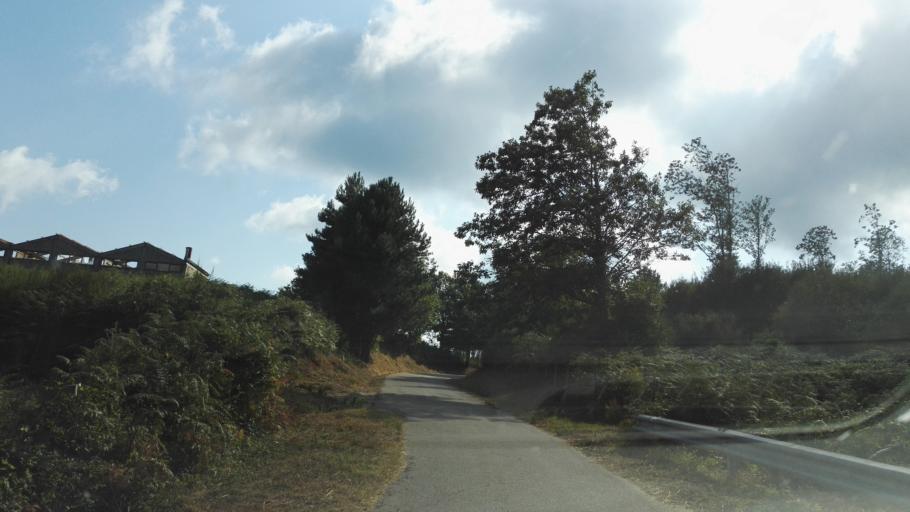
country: IT
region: Calabria
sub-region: Provincia di Vibo-Valentia
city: Nardodipace
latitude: 38.4774
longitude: 16.3448
